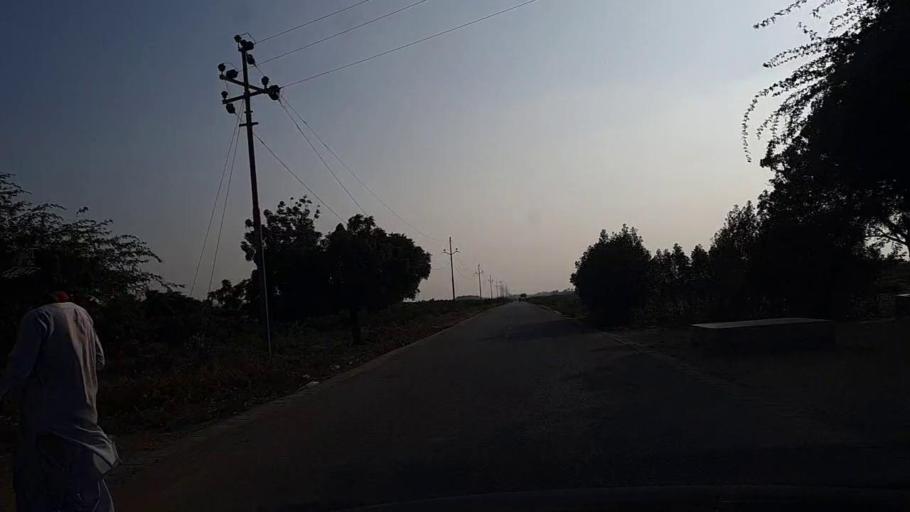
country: PK
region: Sindh
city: Gharo
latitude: 24.7966
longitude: 67.5186
